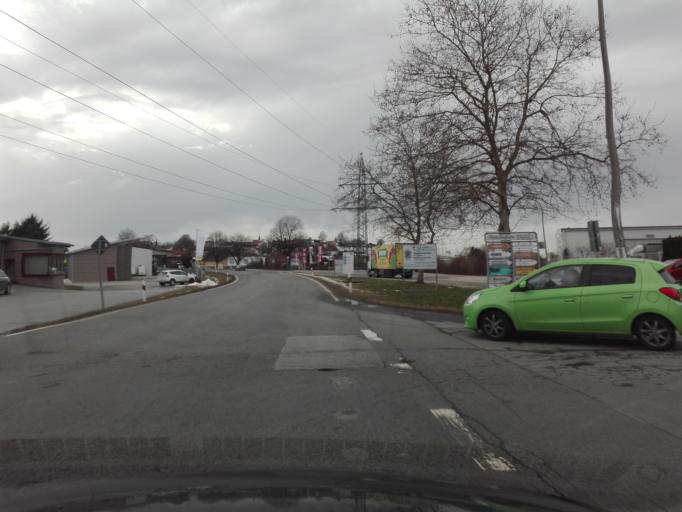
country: DE
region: Bavaria
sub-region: Lower Bavaria
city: Untergriesbach
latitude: 48.5735
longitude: 13.6814
